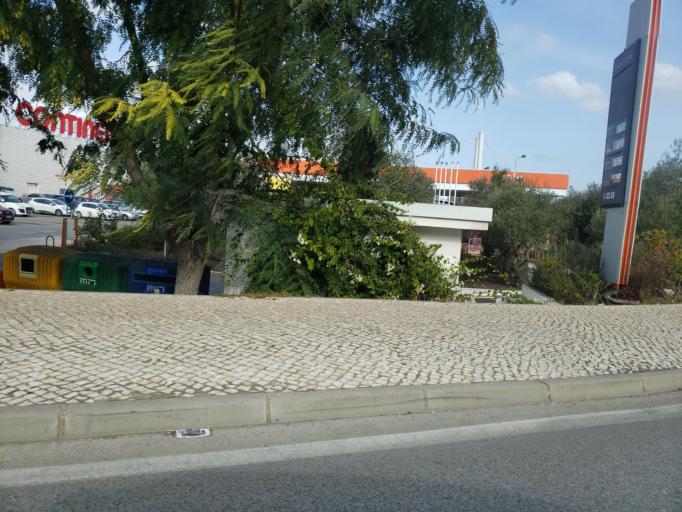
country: PT
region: Faro
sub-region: Portimao
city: Portimao
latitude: 37.1510
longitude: -8.5522
